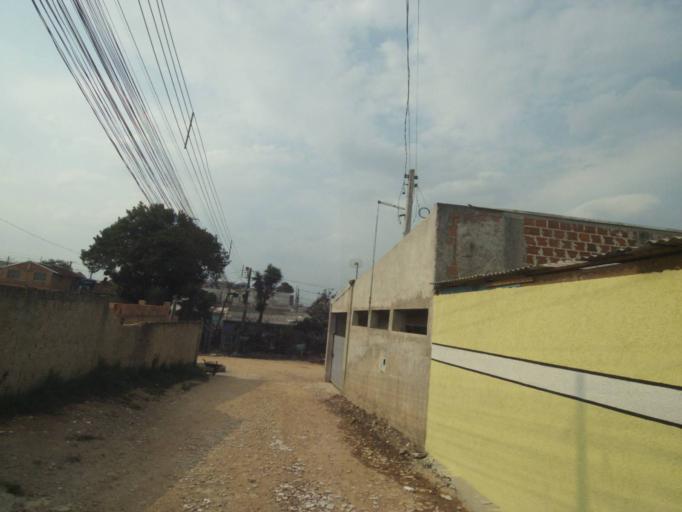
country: BR
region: Parana
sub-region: Sao Jose Dos Pinhais
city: Sao Jose dos Pinhais
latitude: -25.5394
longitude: -49.2325
